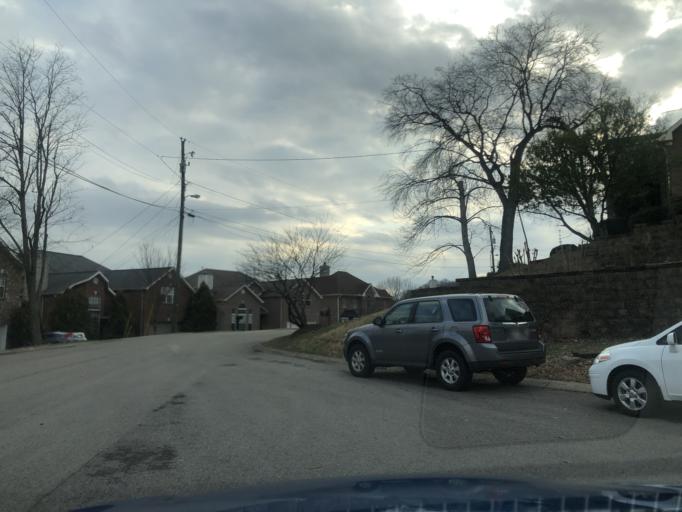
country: US
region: Tennessee
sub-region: Davidson County
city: Belle Meade
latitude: 36.1044
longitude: -86.9346
